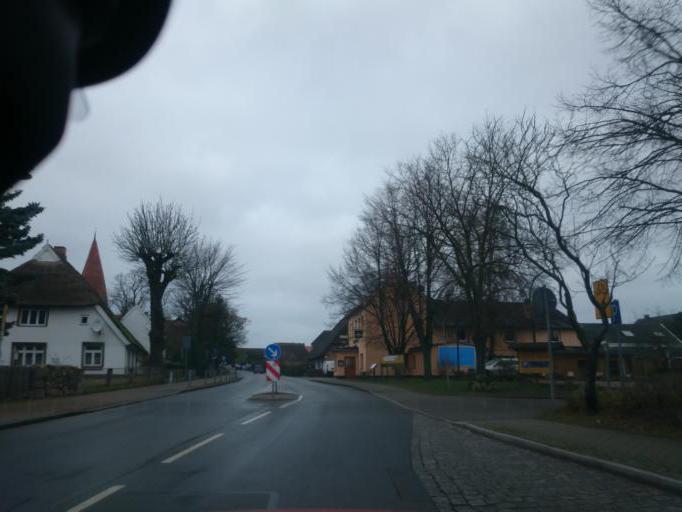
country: DE
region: Mecklenburg-Vorpommern
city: Elmenhorst
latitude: 54.1396
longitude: 12.0327
